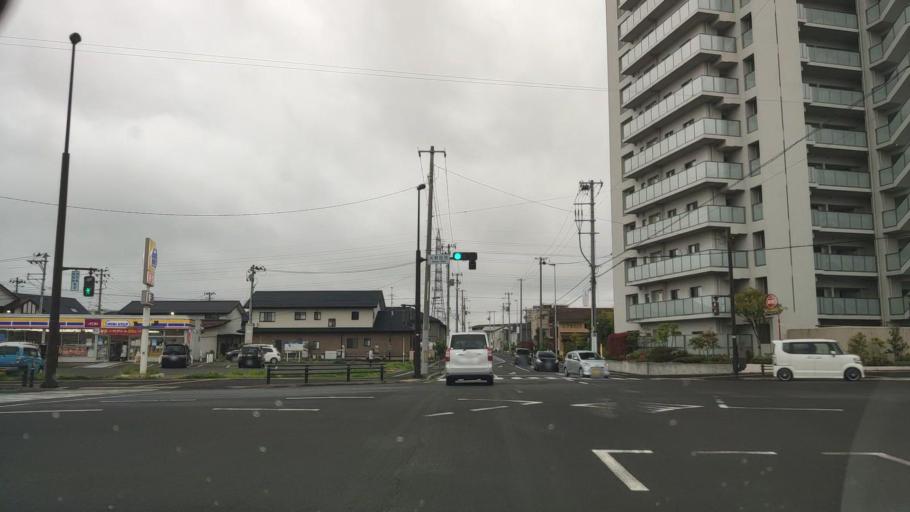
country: JP
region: Miyagi
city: Sendai
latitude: 38.2140
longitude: 140.8735
